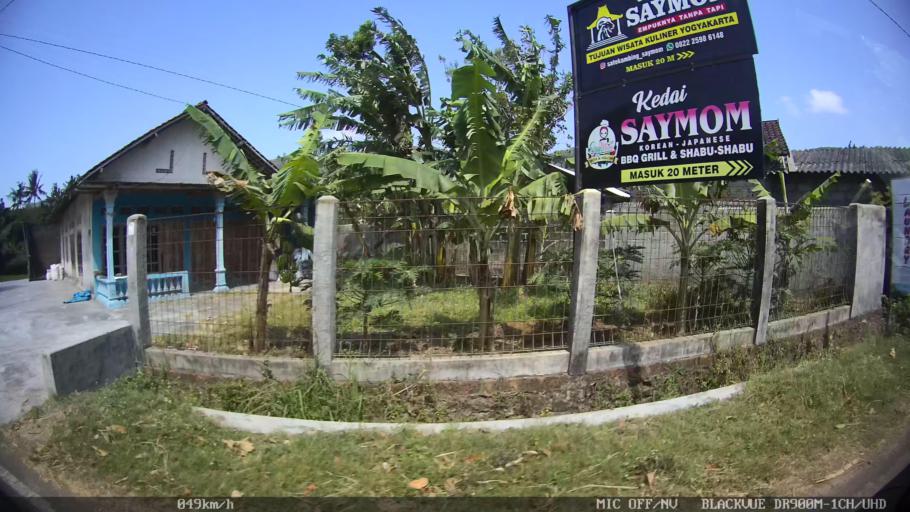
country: ID
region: Daerah Istimewa Yogyakarta
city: Pundong
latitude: -7.9812
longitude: 110.3369
